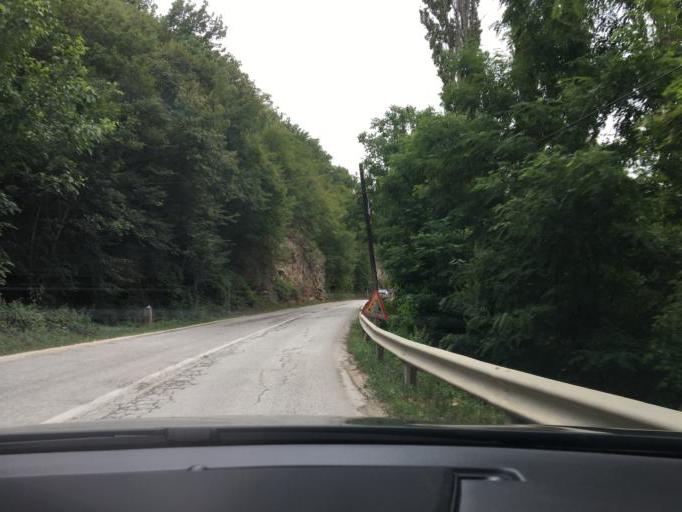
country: MK
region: Kriva Palanka
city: Kriva Palanka
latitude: 42.2146
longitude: 22.3490
